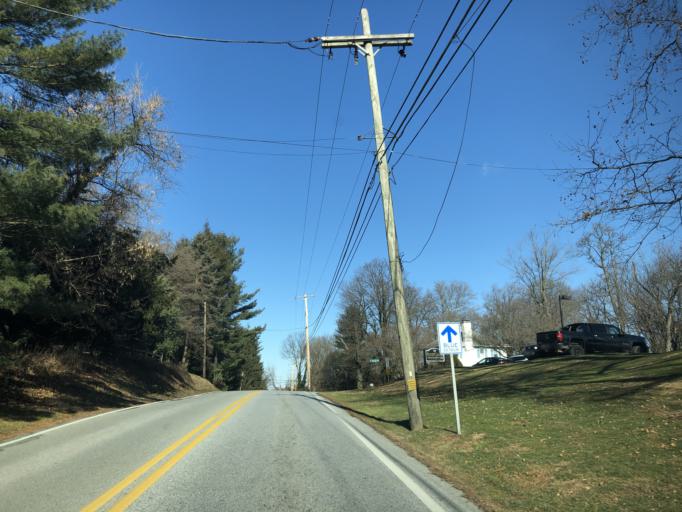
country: US
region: Pennsylvania
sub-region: Chester County
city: Kennett Square
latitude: 39.8653
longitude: -75.7168
